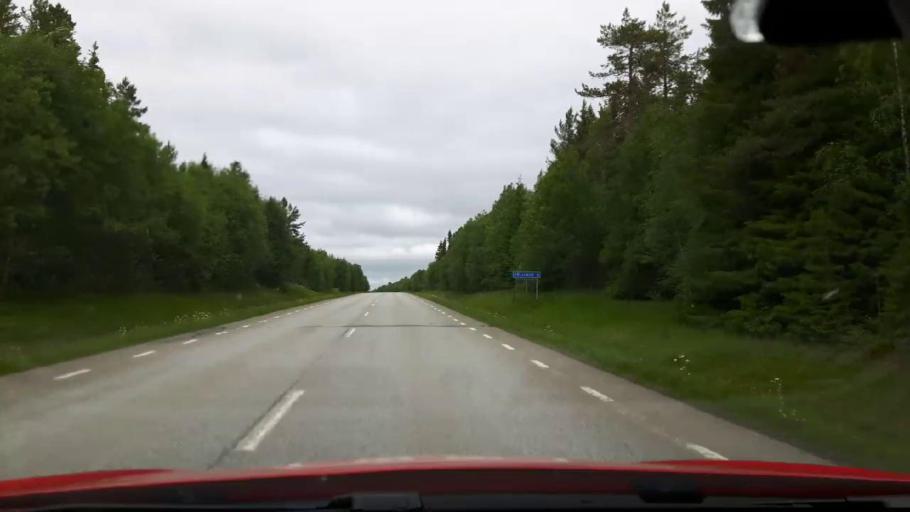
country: SE
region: Jaemtland
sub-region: OEstersunds Kommun
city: Lit
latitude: 63.6148
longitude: 14.6751
